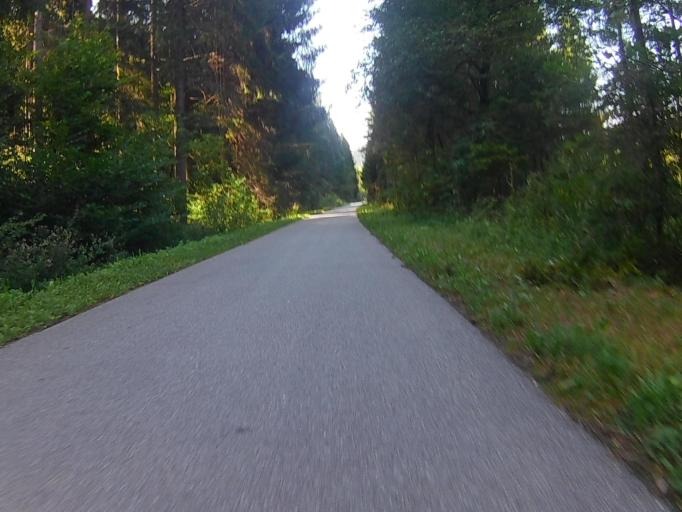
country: SI
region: Mislinja
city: Mislinja
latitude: 46.4372
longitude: 15.1943
